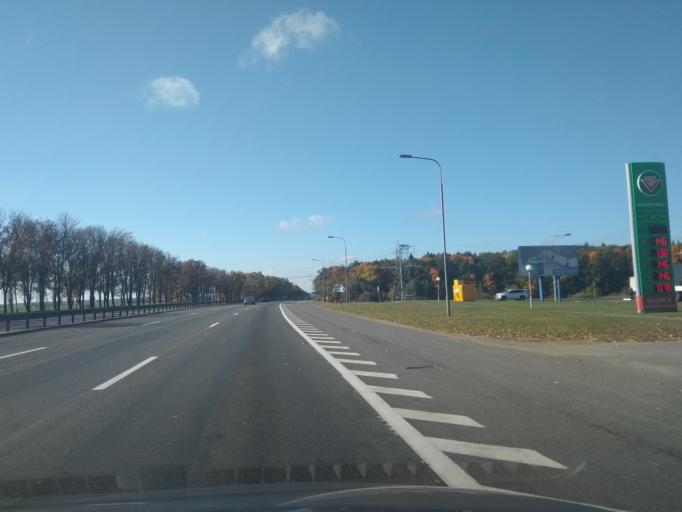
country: BY
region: Minsk
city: Shchomyslitsa
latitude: 53.8173
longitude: 27.4302
